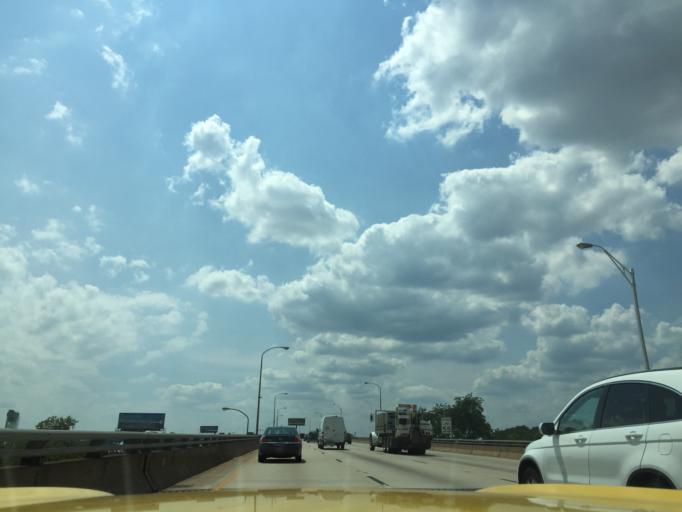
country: US
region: New Jersey
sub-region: Gloucester County
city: National Park
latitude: 39.8983
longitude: -75.1826
